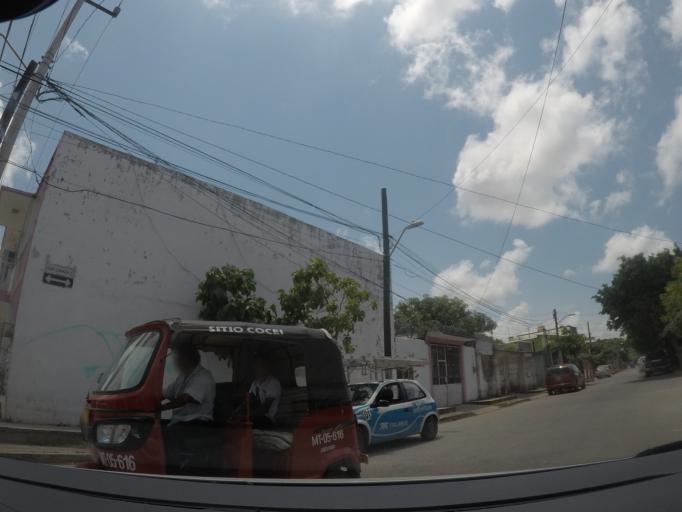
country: MX
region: Oaxaca
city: Juchitan de Zaragoza
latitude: 16.4412
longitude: -95.0112
